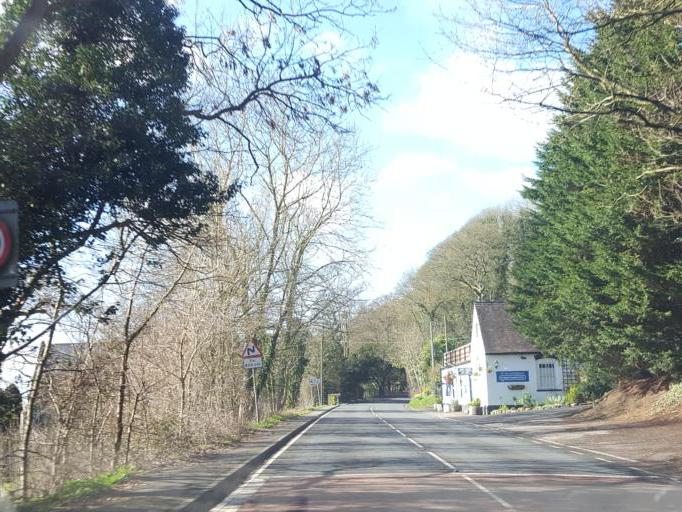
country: GB
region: England
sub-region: Worcestershire
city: Great Malvern
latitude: 52.0679
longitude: -2.3351
